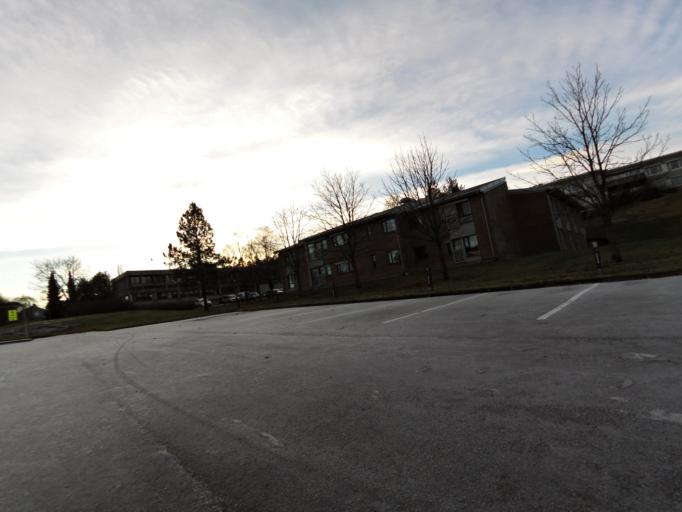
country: NO
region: Ostfold
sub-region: Fredrikstad
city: Fredrikstad
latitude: 59.2307
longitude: 10.9097
